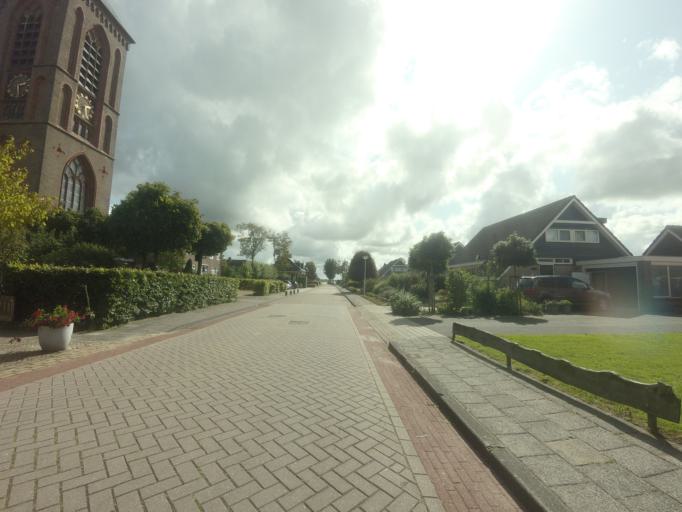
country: NL
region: Friesland
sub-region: Sudwest Fryslan
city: Scharnegoutum
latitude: 53.0765
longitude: 5.6362
